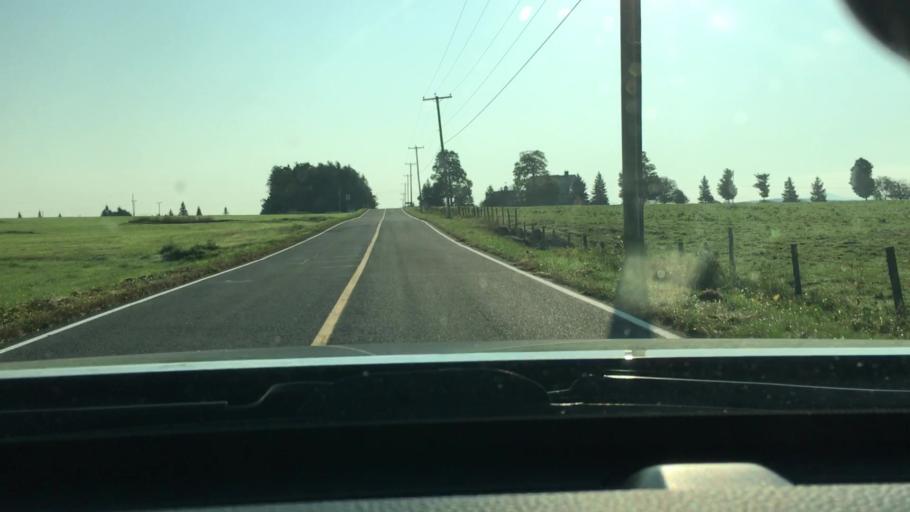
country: CA
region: Quebec
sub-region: Monteregie
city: Waterloo
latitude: 45.3557
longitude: -72.4938
